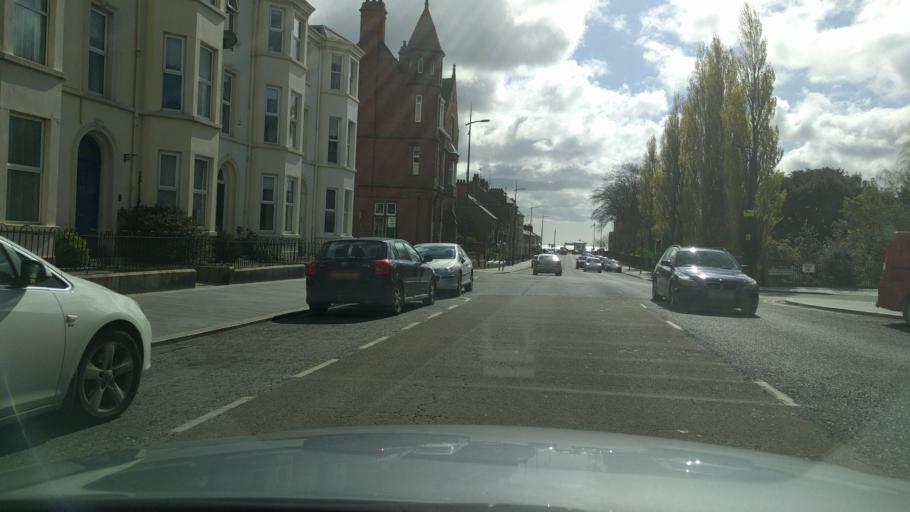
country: GB
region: Northern Ireland
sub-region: Down District
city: Warrenpoint
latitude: 54.1001
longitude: -6.2518
